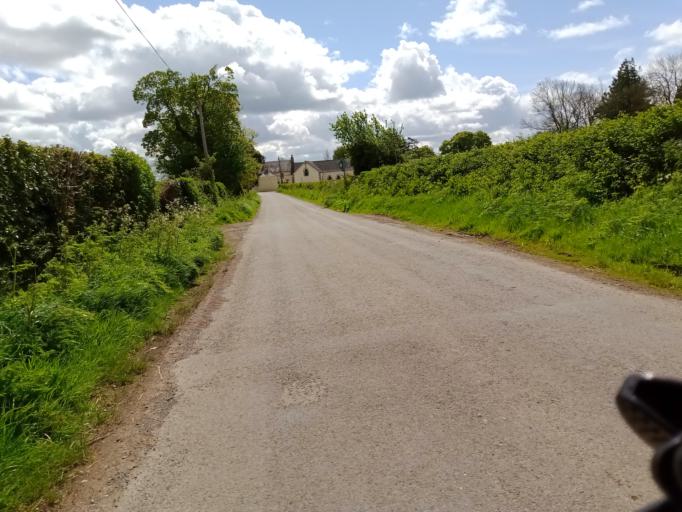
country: IE
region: Leinster
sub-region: Kilkenny
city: Thomastown
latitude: 52.5799
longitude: -7.1286
